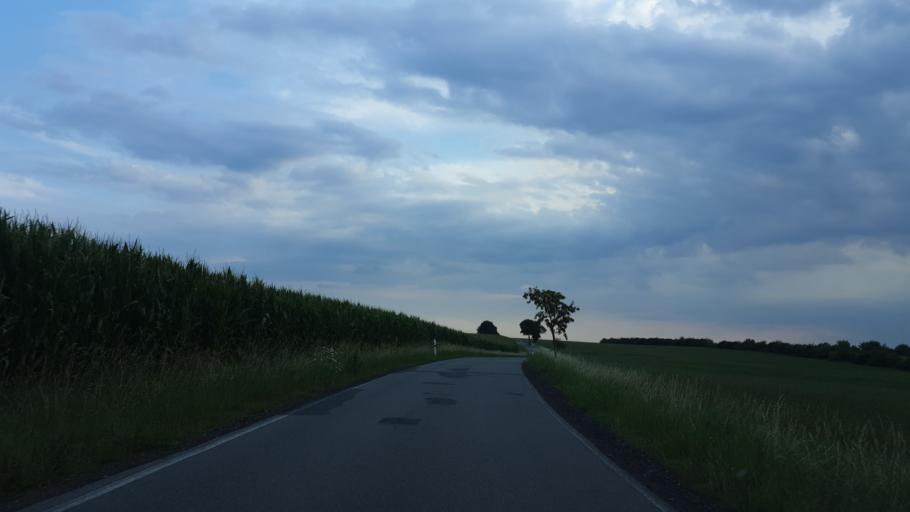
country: DE
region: Saxony
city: Kirchberg
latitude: 50.7598
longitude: 12.7361
